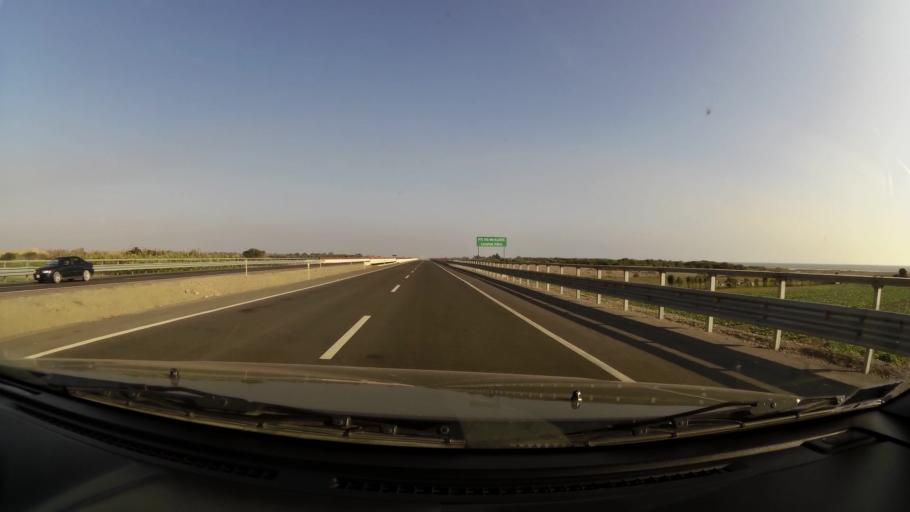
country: PE
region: Ica
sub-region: Provincia de Chincha
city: Chincha Baja
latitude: -13.5243
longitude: -76.1831
